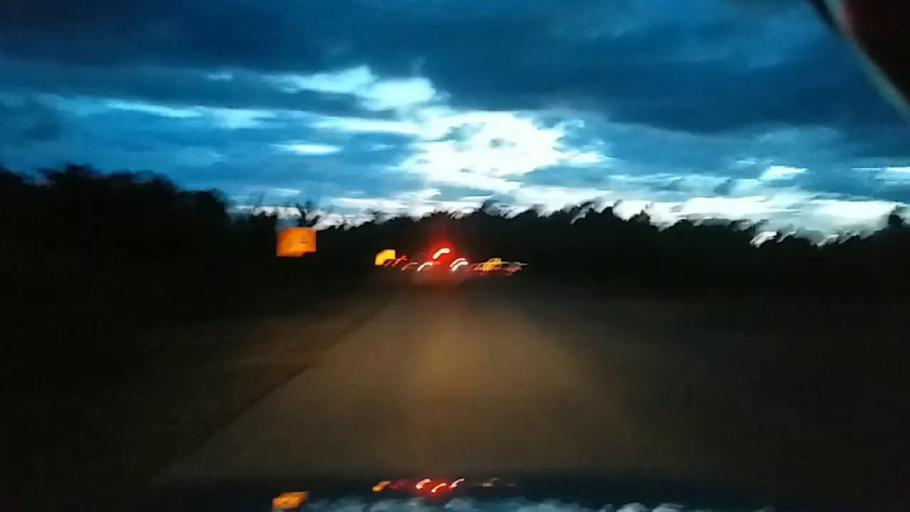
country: MY
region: Sarawak
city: Sibu
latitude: 2.4135
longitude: 112.1579
